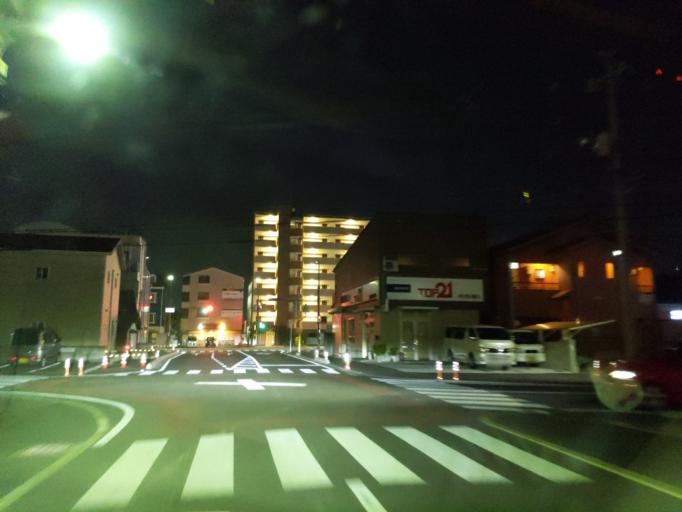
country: JP
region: Okayama
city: Okayama-shi
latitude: 34.6819
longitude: 133.9112
